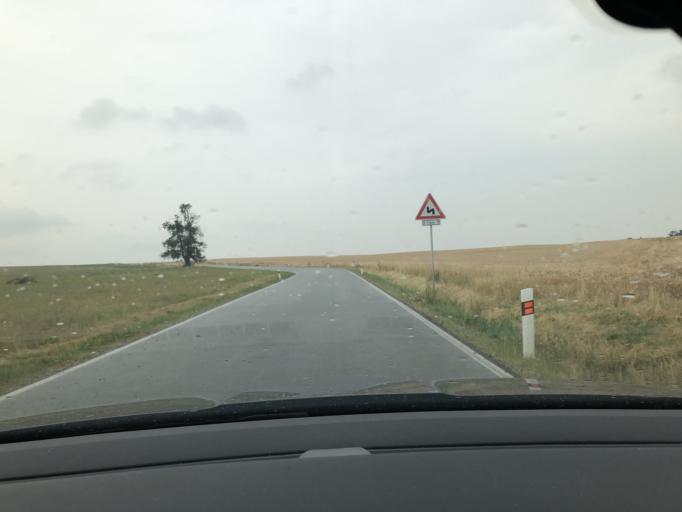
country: CZ
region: South Moravian
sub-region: Okres Znojmo
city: Jevisovice
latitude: 49.0281
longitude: 15.9970
